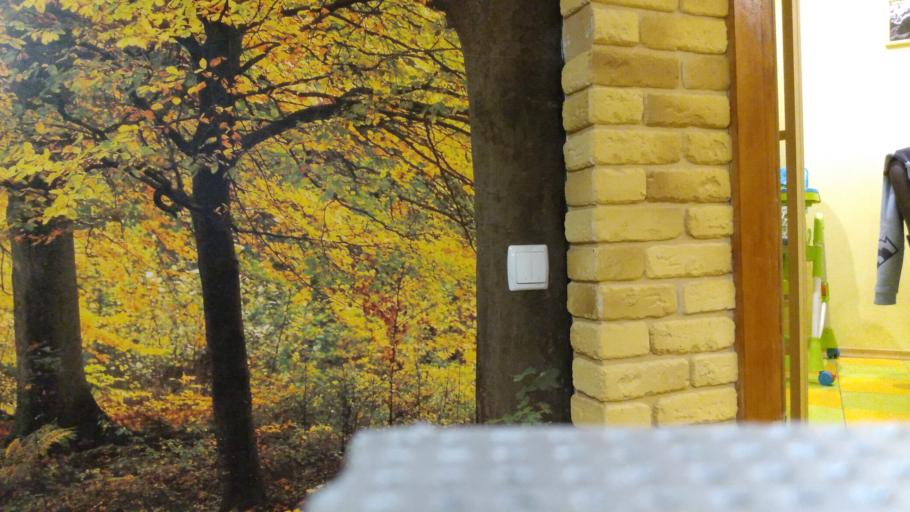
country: RU
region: Vologda
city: Babayevo
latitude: 59.3623
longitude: 36.0013
